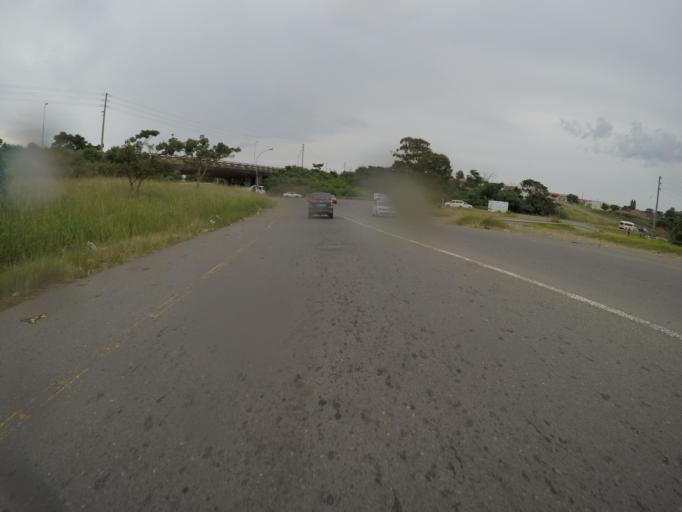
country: ZA
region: Eastern Cape
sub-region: Buffalo City Metropolitan Municipality
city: East London
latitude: -33.0005
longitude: 27.8423
